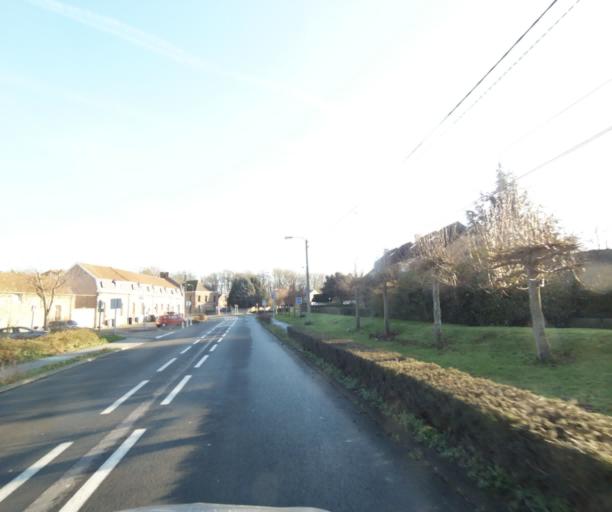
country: FR
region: Nord-Pas-de-Calais
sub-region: Departement du Nord
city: Saultain
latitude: 50.3371
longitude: 3.5734
